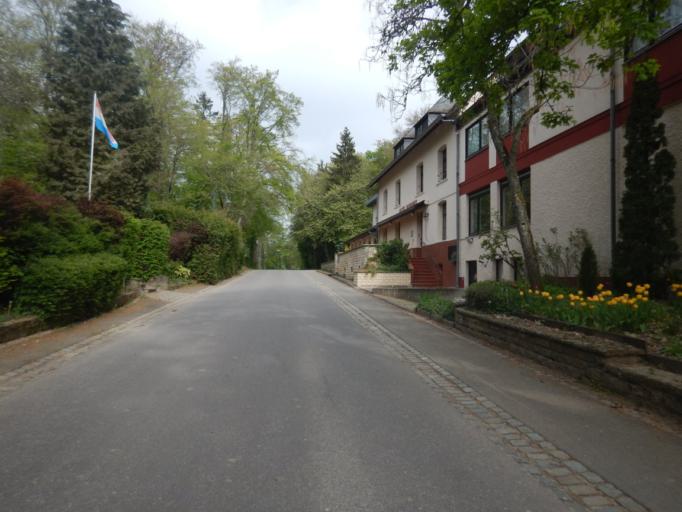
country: LU
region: Grevenmacher
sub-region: Canton d'Echternach
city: Berdorf
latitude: 49.8111
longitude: 6.3489
